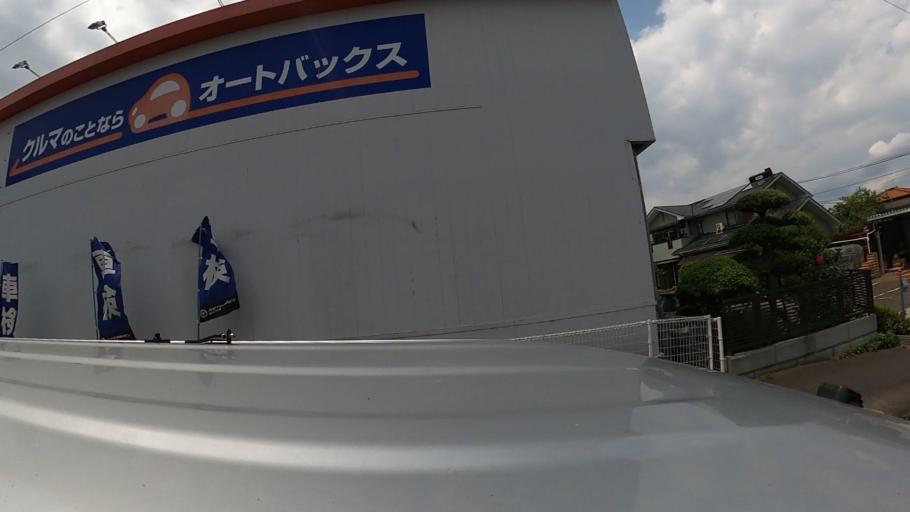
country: JP
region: Kanagawa
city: Chigasaki
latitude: 35.3769
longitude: 139.3968
